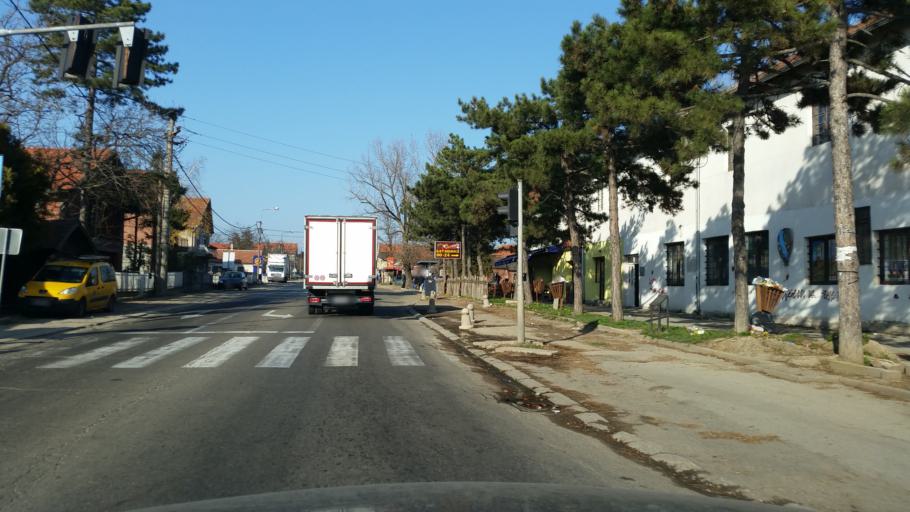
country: RS
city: Stepojevac
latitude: 44.5137
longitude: 20.2945
